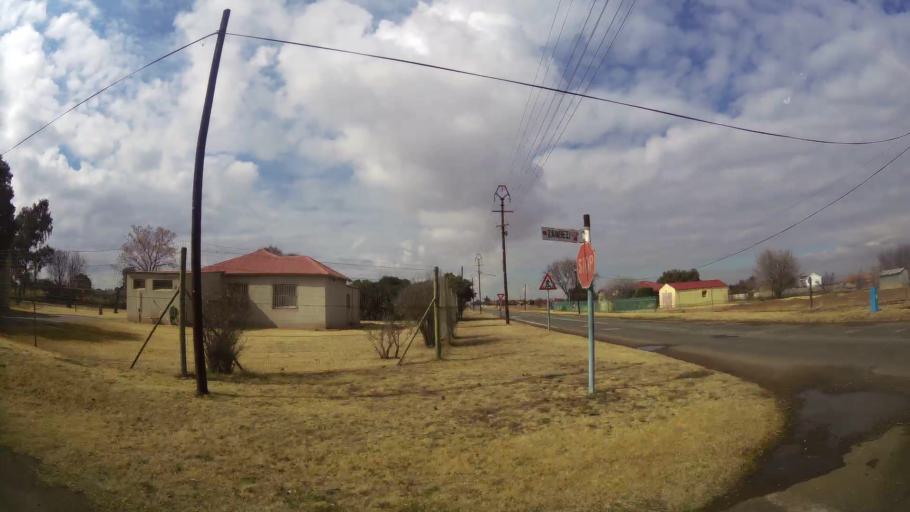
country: ZA
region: Gauteng
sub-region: Sedibeng District Municipality
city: Meyerton
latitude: -26.6064
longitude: 28.0510
